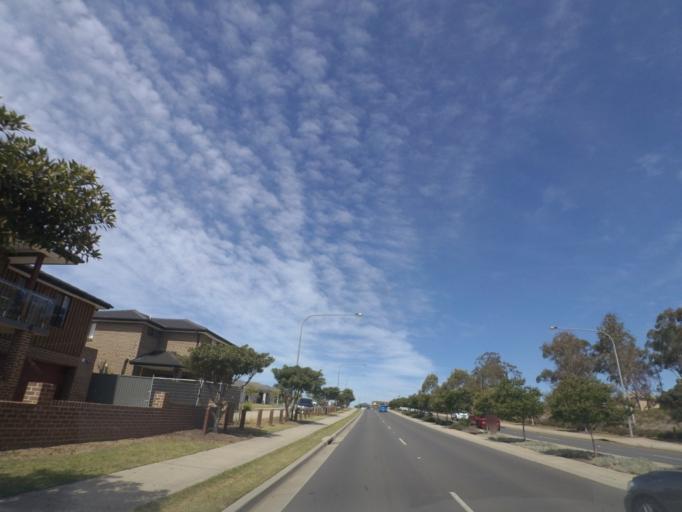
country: AU
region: New South Wales
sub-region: Camden
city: Narellan Vale
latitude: -34.0251
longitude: 150.7732
